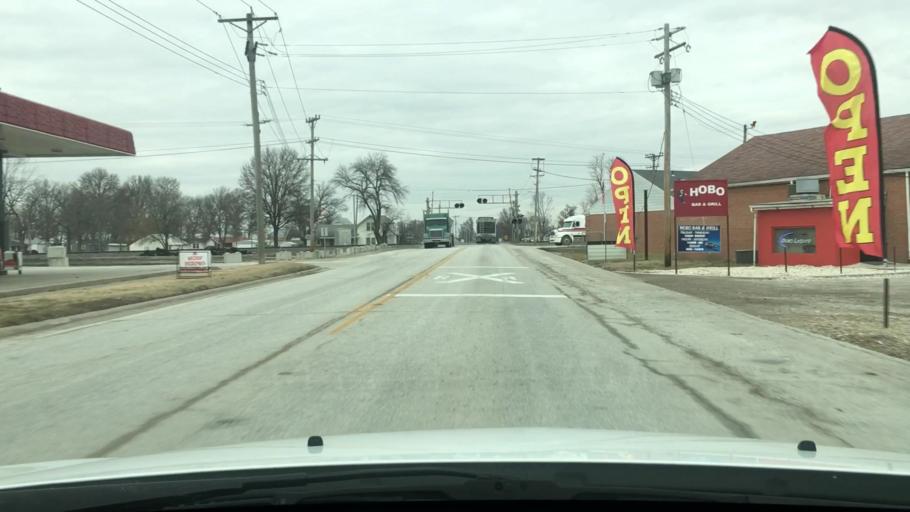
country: US
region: Missouri
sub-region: Audrain County
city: Vandalia
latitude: 39.2413
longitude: -91.6456
